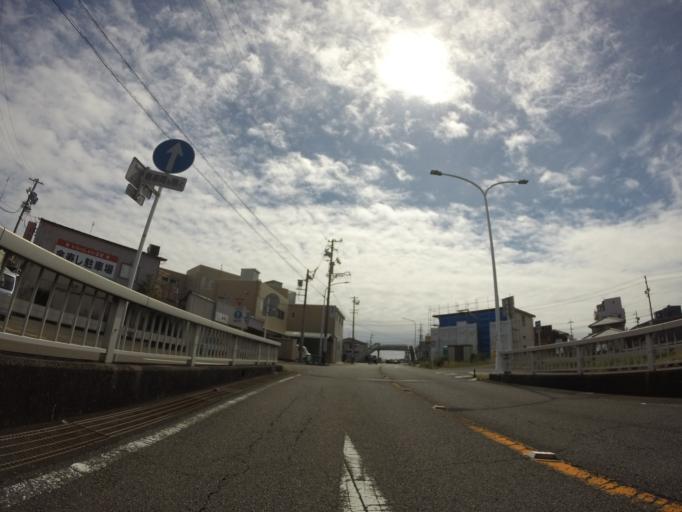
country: JP
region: Shizuoka
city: Yaizu
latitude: 34.8737
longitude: 138.3238
